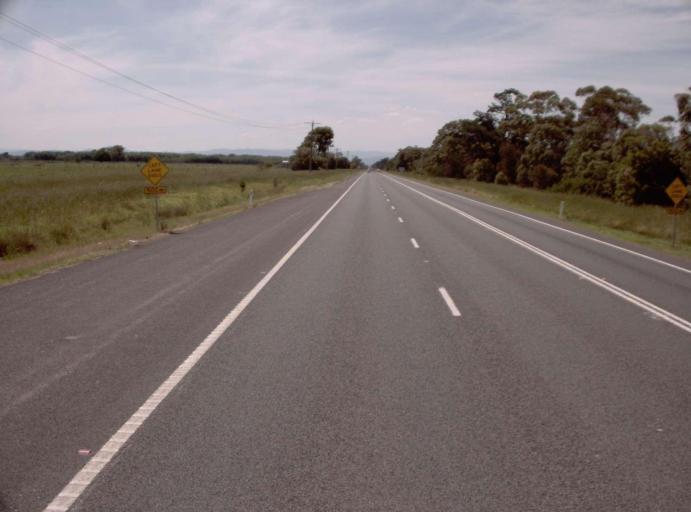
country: AU
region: Victoria
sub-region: Wellington
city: Sale
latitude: -38.0646
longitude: 147.0723
